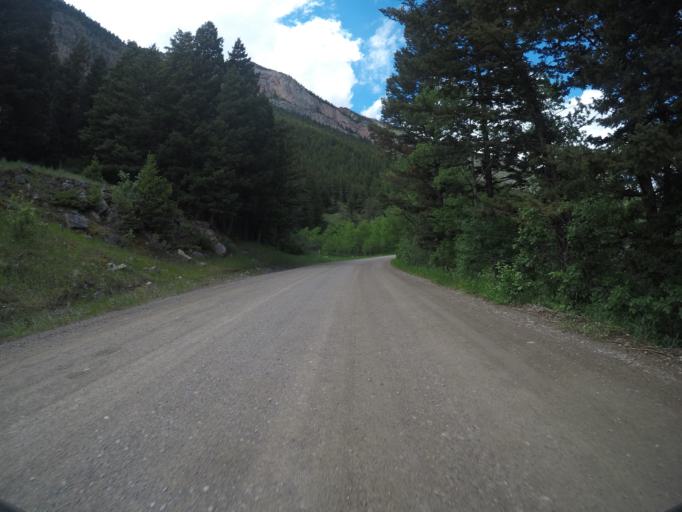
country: US
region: Montana
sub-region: Park County
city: Livingston
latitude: 45.5391
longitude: -110.2146
